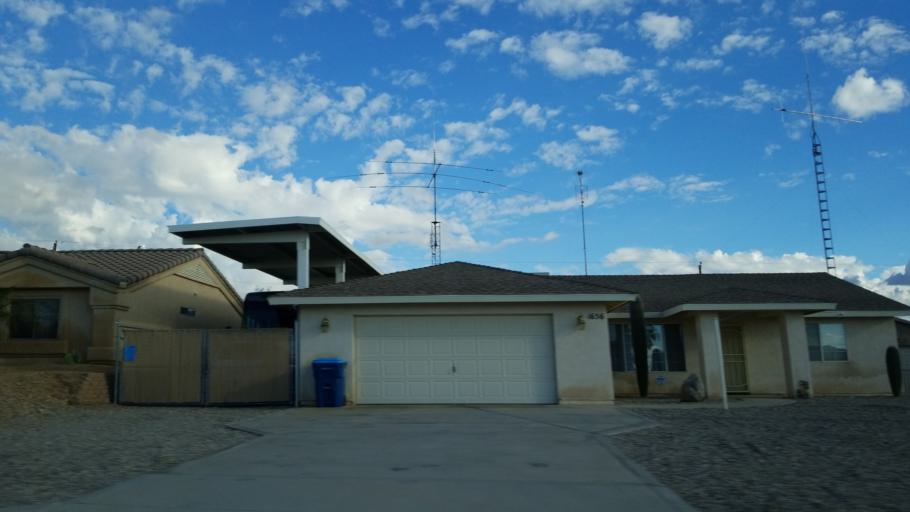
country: US
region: Arizona
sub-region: Mohave County
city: Lake Havasu City
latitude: 34.4564
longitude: -114.2606
